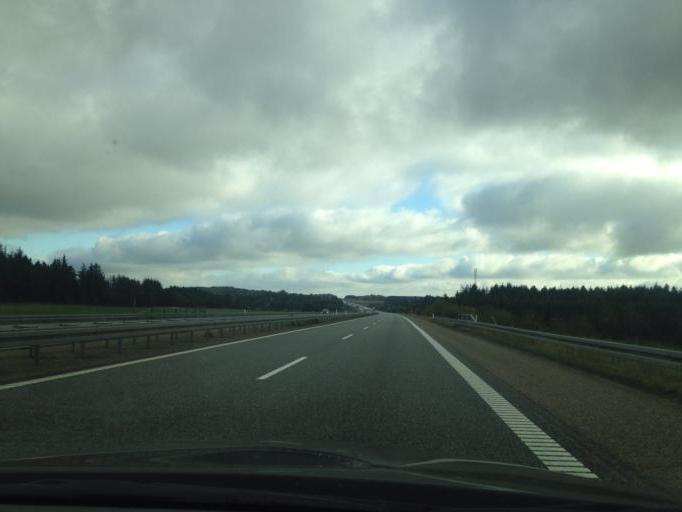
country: DK
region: South Denmark
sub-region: Vejle Kommune
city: Give
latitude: 55.8341
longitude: 9.3295
